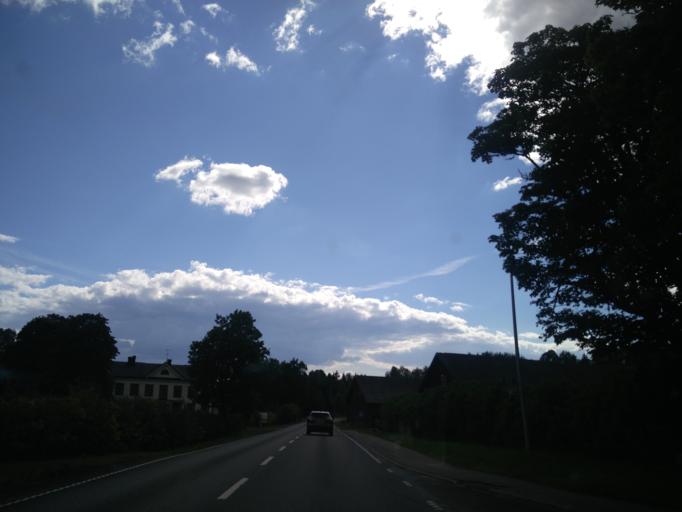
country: SE
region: OErebro
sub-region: Hallefors Kommun
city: Haellefors
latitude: 59.8012
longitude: 14.5841
